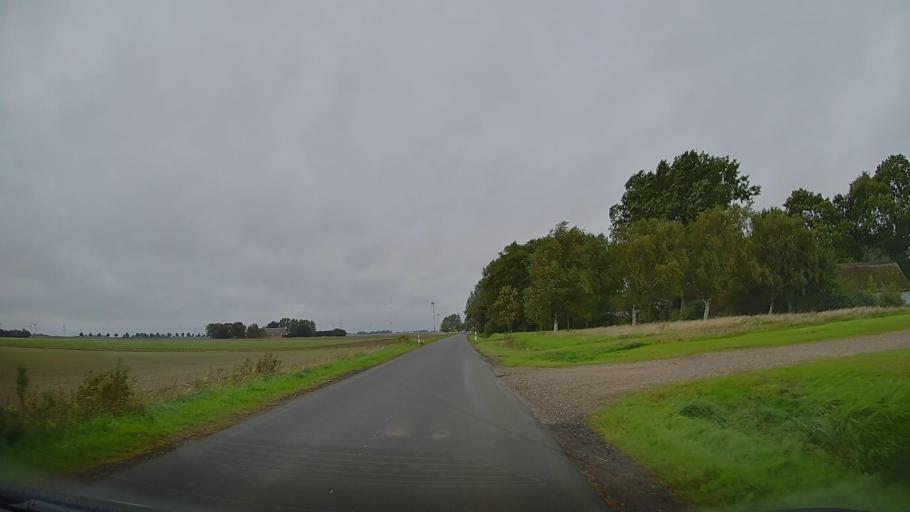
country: DE
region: Schleswig-Holstein
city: Marnerdeich
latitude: 53.9258
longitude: 8.9846
